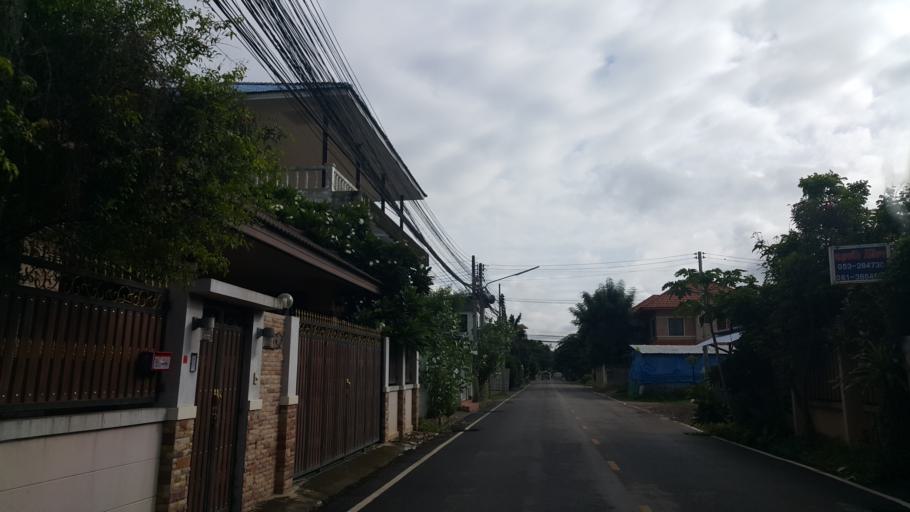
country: TH
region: Chiang Mai
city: Chiang Mai
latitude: 18.7440
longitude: 98.9704
